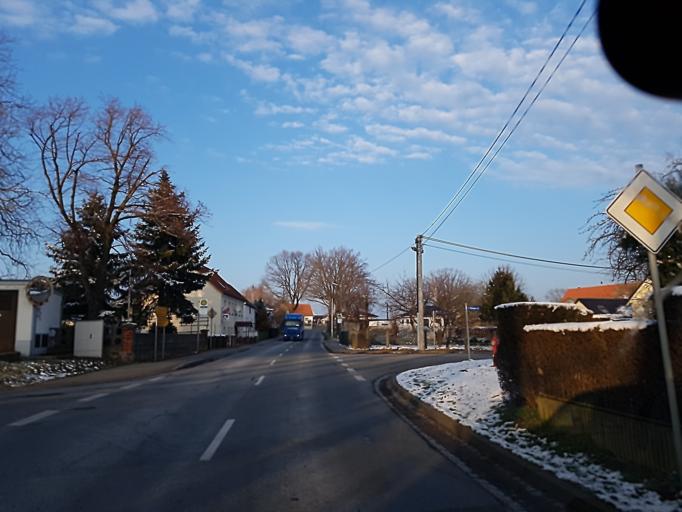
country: DE
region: Saxony
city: Oschatz
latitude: 51.2871
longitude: 13.1366
